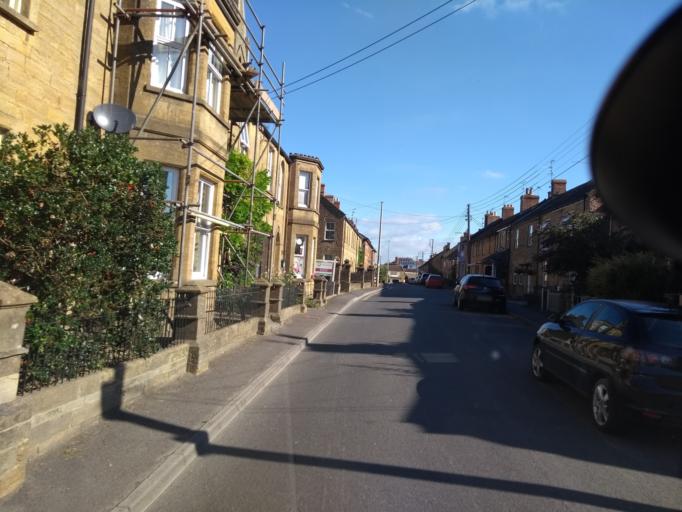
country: GB
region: England
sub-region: Somerset
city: Martock
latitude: 50.9738
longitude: -2.7669
